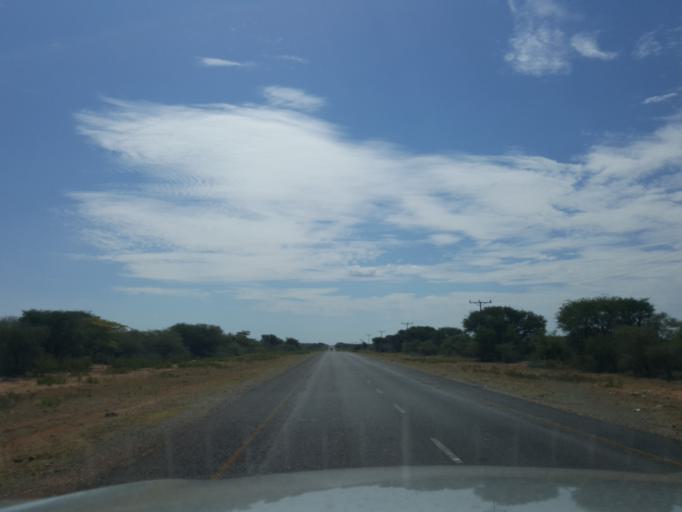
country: BW
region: Kweneng
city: Letlhakeng
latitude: -24.1578
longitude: 25.1642
